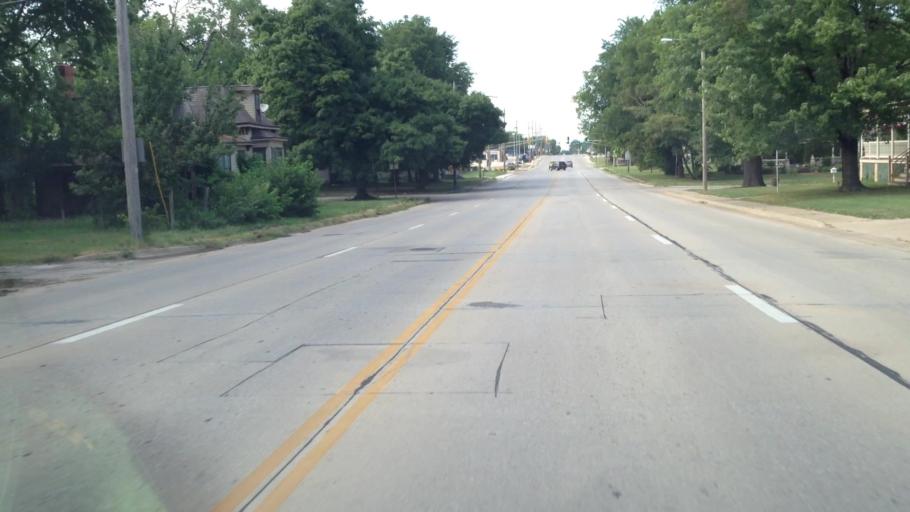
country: US
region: Kansas
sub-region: Labette County
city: Parsons
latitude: 37.3360
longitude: -95.2592
